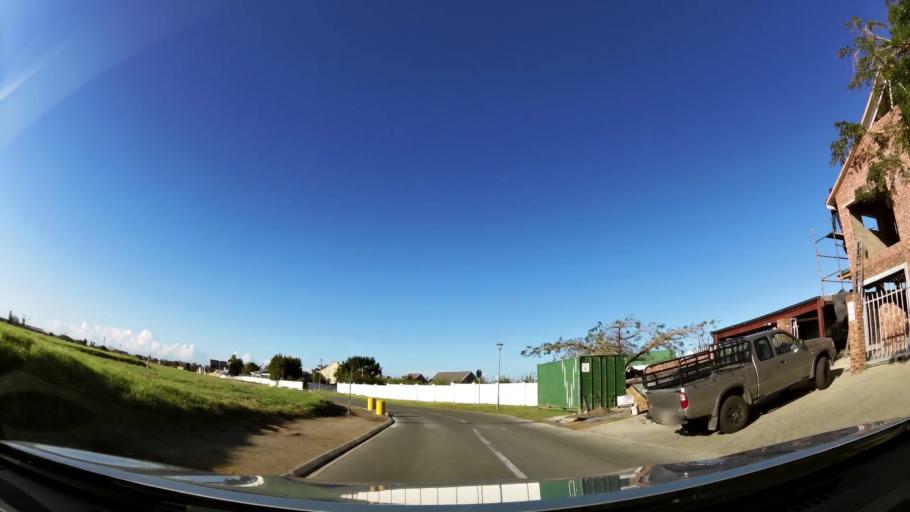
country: ZA
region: Western Cape
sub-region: Eden District Municipality
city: George
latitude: -33.9595
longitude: 22.4441
